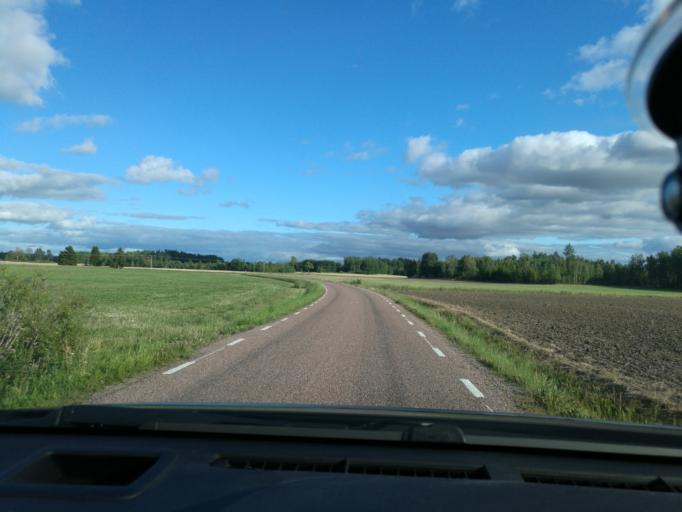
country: SE
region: Vaestmanland
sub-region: Hallstahammars Kommun
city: Hallstahammar
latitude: 59.5460
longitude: 16.1229
